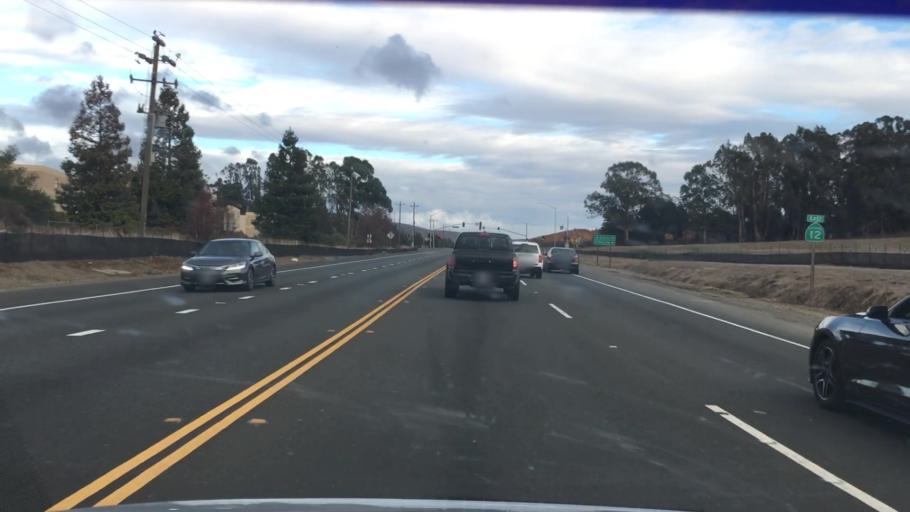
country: US
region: California
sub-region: Napa County
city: American Canyon
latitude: 38.2229
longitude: -122.2562
